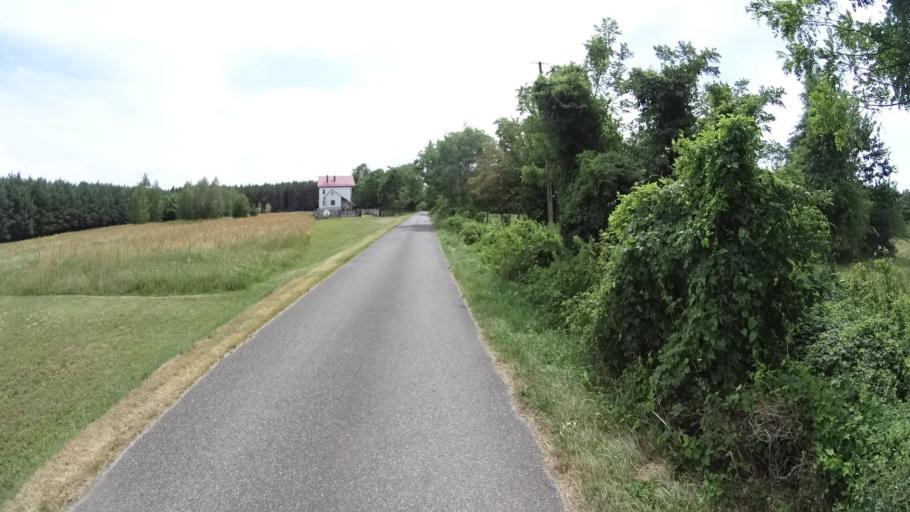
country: PL
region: Masovian Voivodeship
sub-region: Powiat bialobrzeski
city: Bialobrzegi
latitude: 51.6442
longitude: 20.9033
